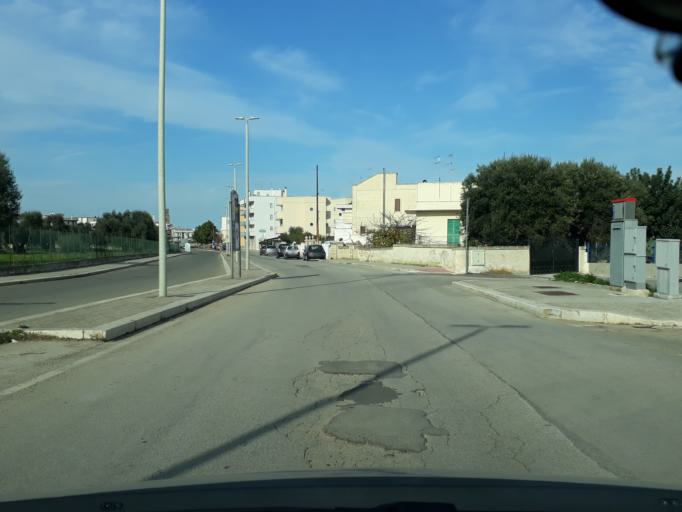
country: IT
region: Apulia
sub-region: Provincia di Brindisi
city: Fasano
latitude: 40.8277
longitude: 17.3606
